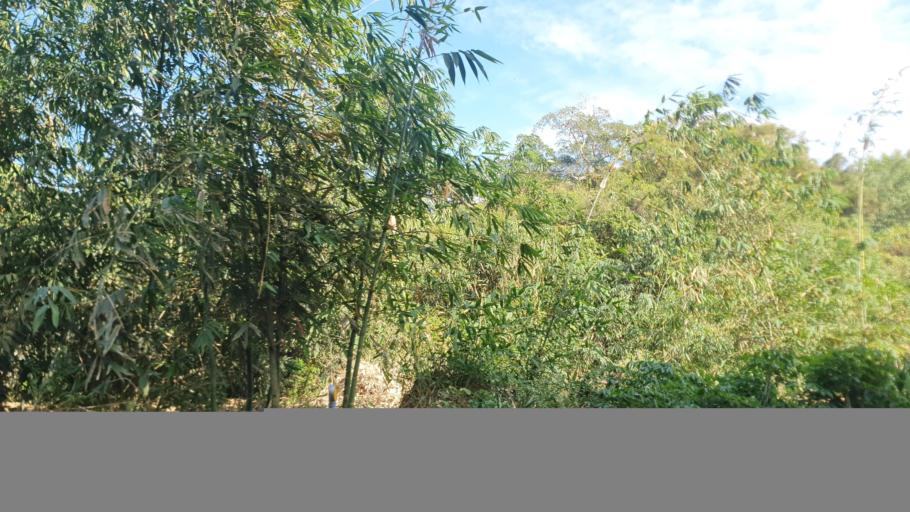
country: TW
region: Taiwan
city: Yujing
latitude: 23.0092
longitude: 120.3871
